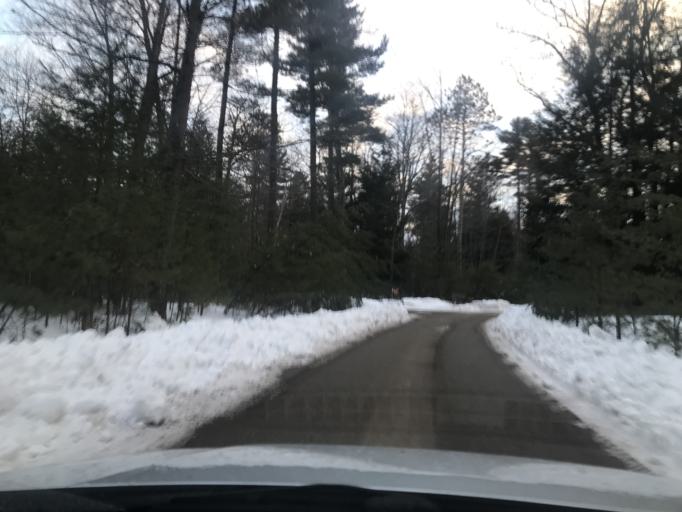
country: US
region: Wisconsin
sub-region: Marinette County
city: Marinette
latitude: 45.1157
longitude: -87.6690
